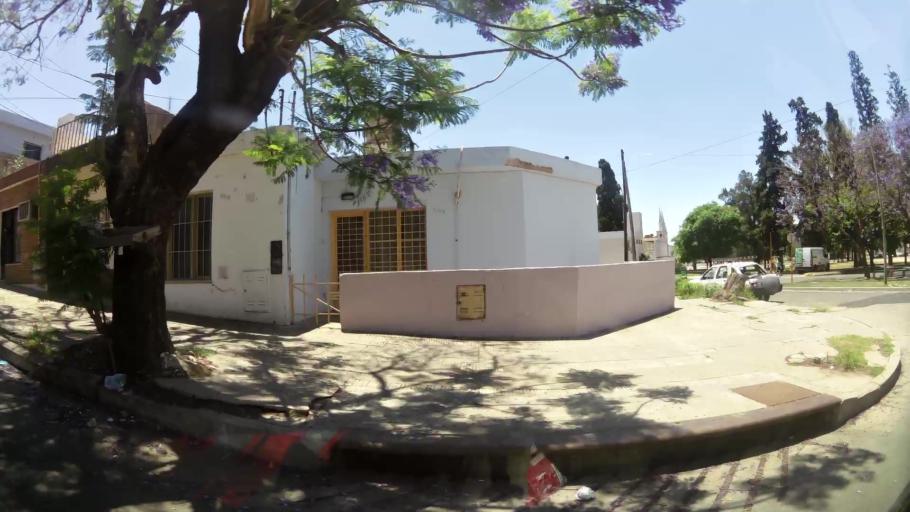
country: AR
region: Cordoba
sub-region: Departamento de Capital
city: Cordoba
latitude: -31.4021
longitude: -64.2140
